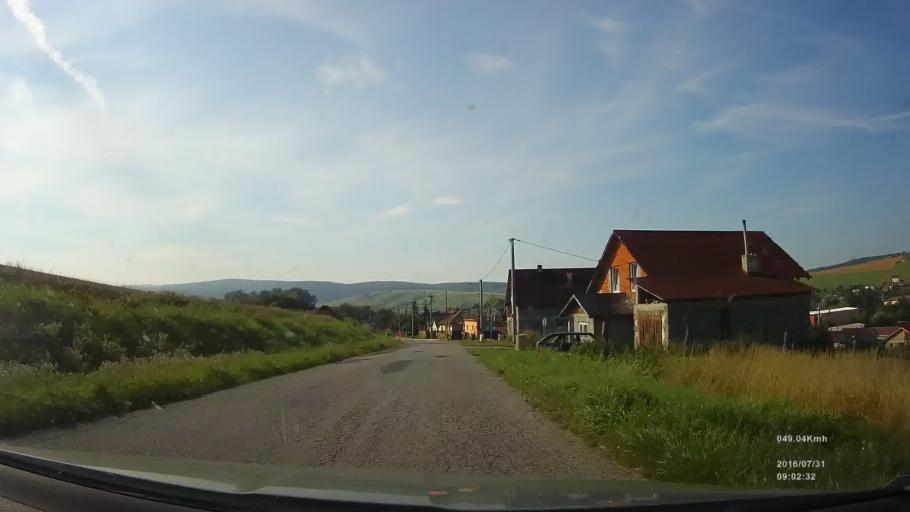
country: SK
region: Presovsky
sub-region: Okres Bardejov
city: Bardejov
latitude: 49.1540
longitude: 21.3233
